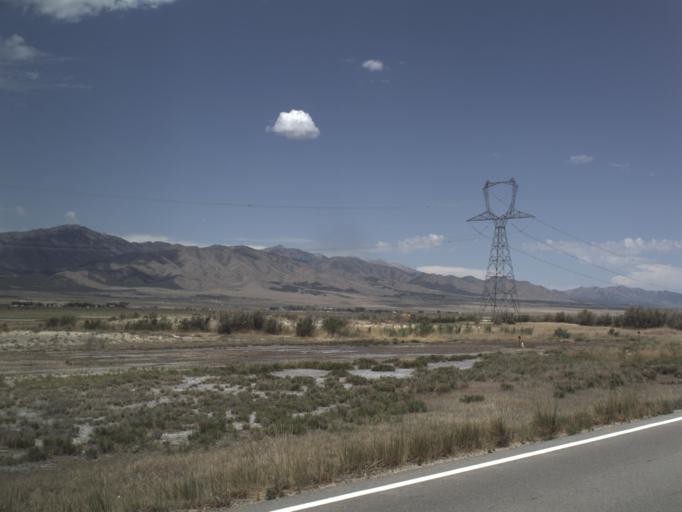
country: US
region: Utah
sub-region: Tooele County
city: Tooele
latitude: 40.3196
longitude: -112.4062
